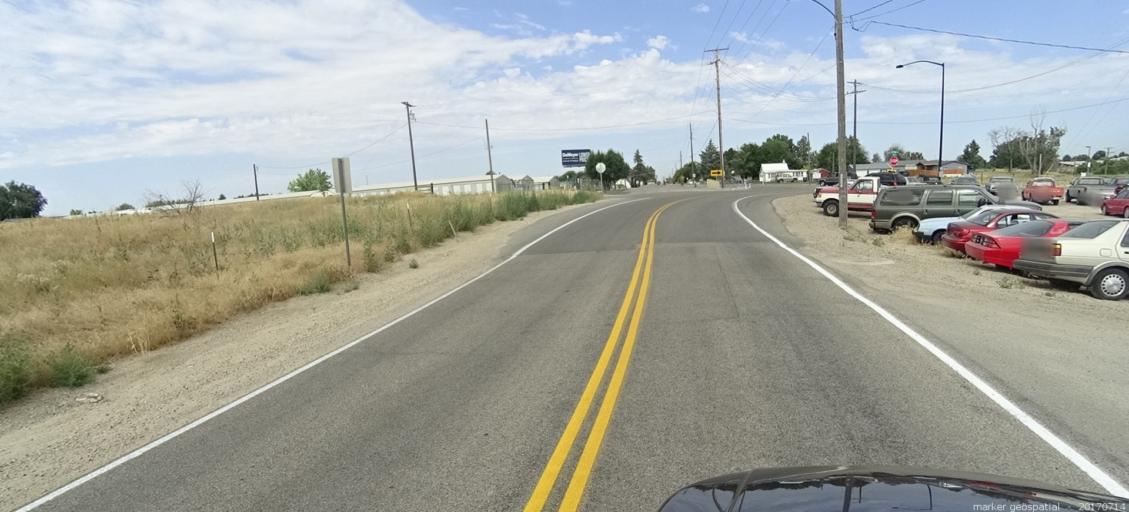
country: US
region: Idaho
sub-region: Ada County
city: Kuna
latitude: 43.4884
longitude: -116.4204
